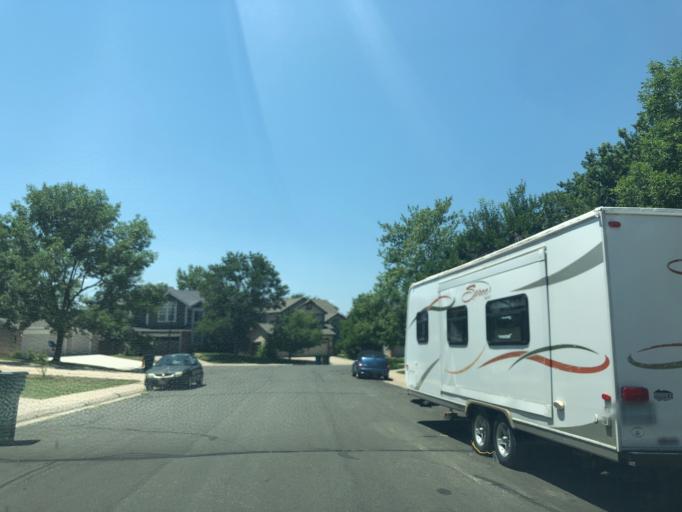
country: US
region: Colorado
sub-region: Arapahoe County
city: Dove Valley
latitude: 39.6271
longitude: -104.7673
